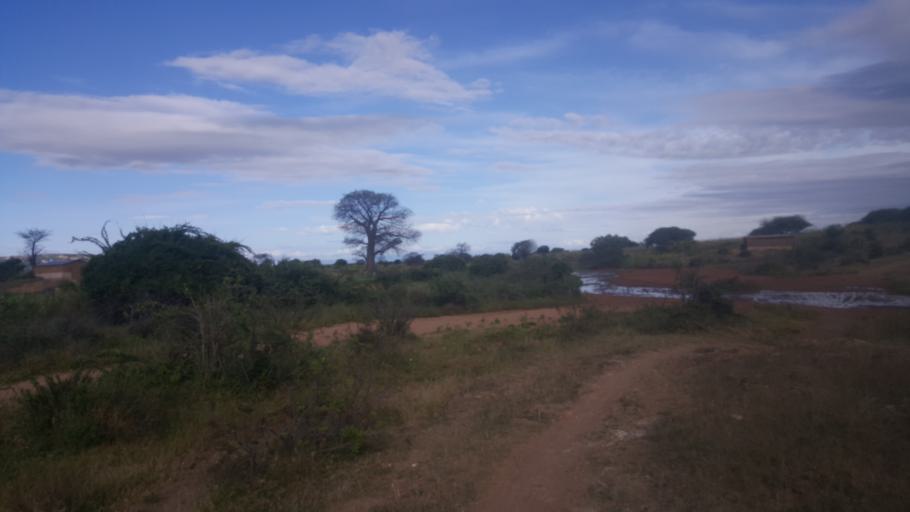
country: TZ
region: Dodoma
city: Dodoma
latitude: -6.0988
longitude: 35.5354
